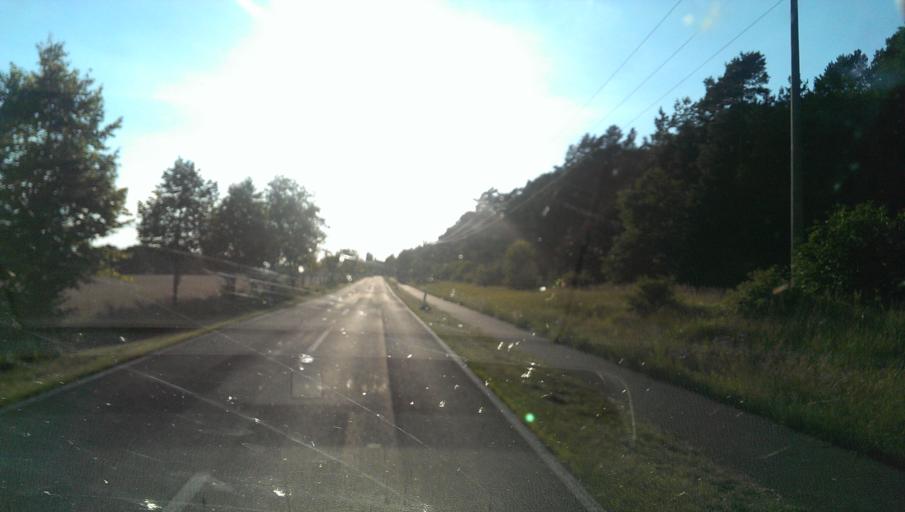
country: DE
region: Brandenburg
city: Trebbin
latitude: 52.2368
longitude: 13.1842
